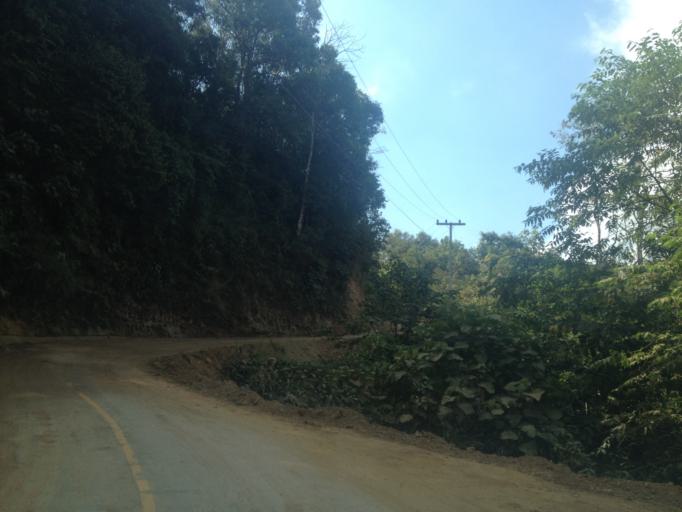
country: TH
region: Mae Hong Son
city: Ban Huai I Huak
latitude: 18.1210
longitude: 98.1461
